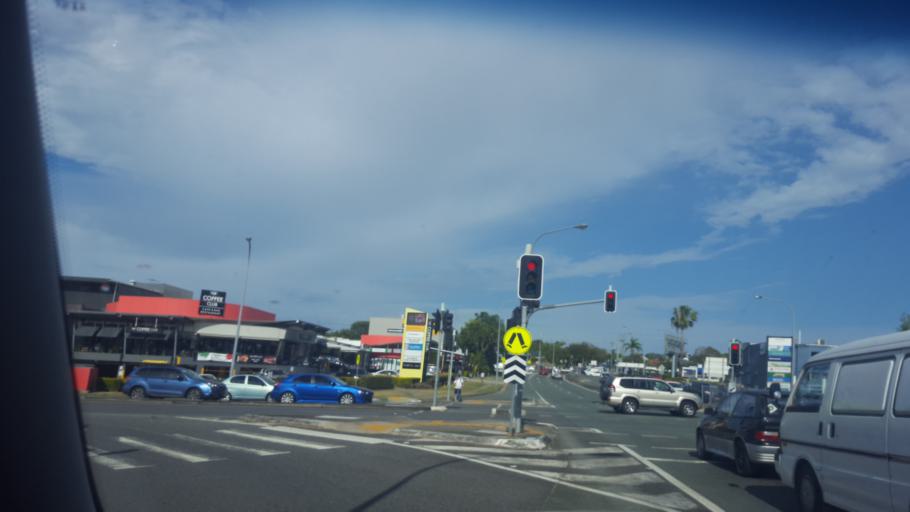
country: AU
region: Queensland
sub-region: Brisbane
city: Chermside West
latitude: -27.3638
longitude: 153.0153
